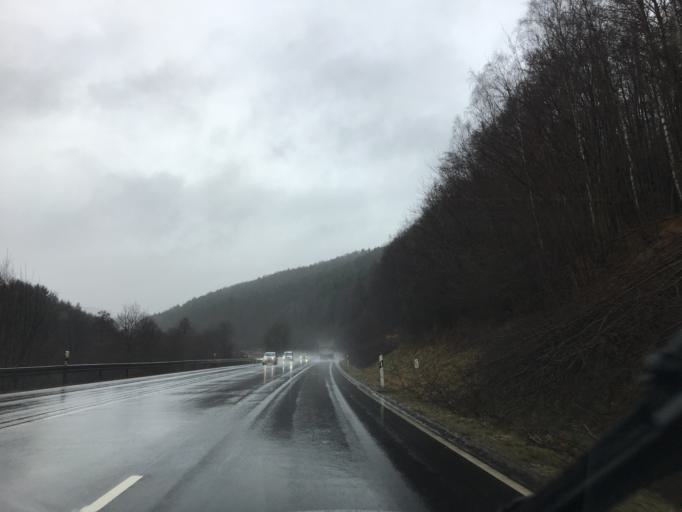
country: DE
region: Hesse
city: Michelstadt
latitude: 49.7025
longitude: 8.9986
